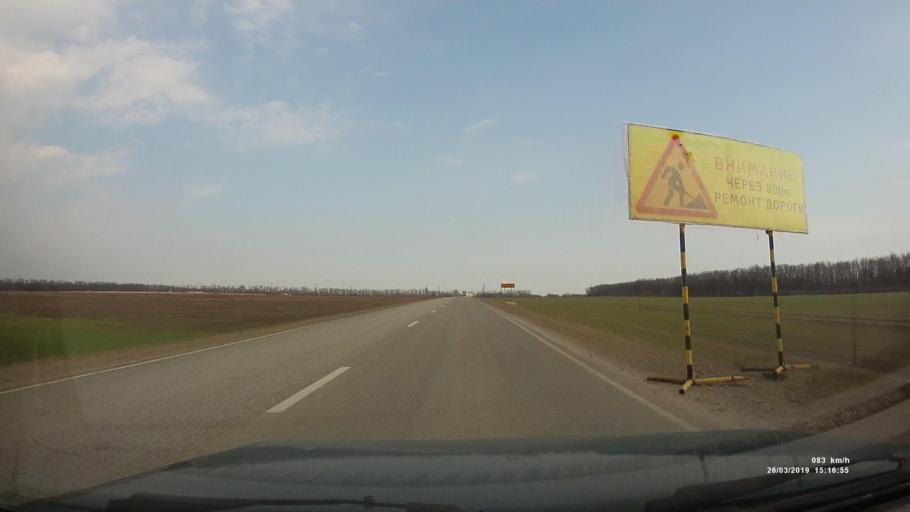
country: RU
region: Rostov
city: Taganrog
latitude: 47.2865
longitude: 38.9110
